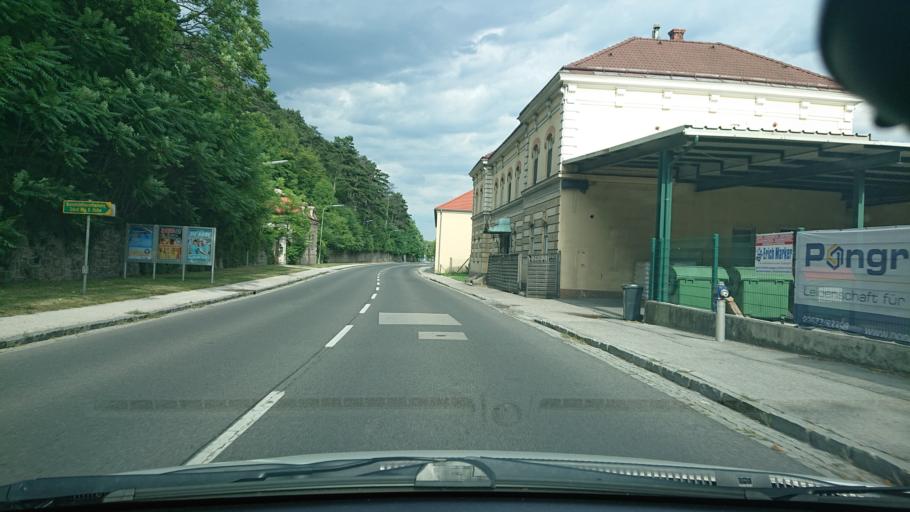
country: AT
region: Lower Austria
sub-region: Politischer Bezirk Baden
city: Berndorf
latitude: 47.9428
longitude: 16.1142
